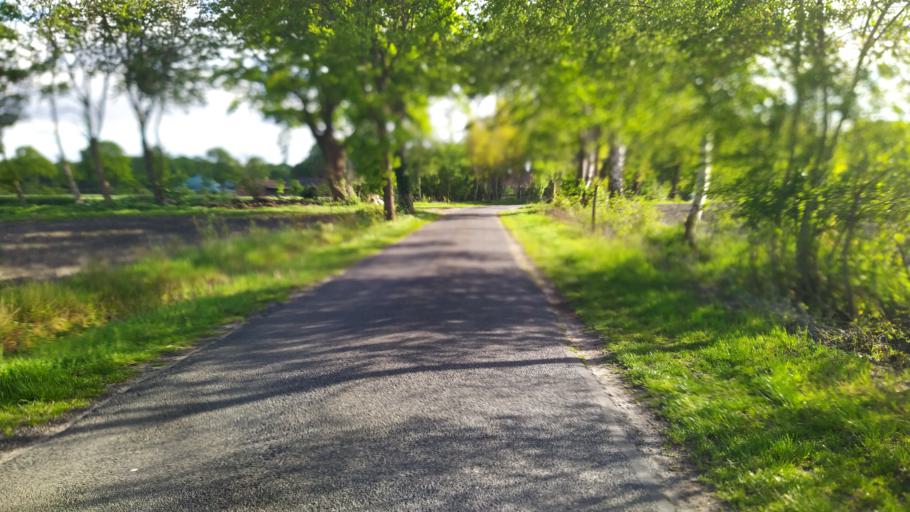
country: DE
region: Lower Saxony
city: Brest
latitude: 53.4053
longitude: 9.3630
